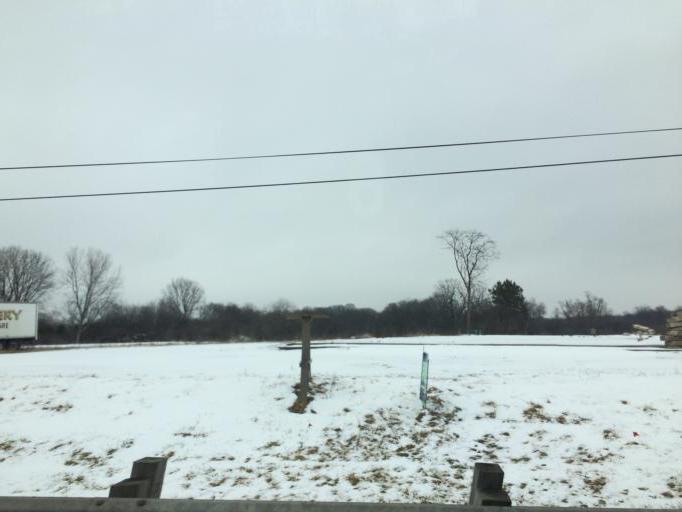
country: US
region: Illinois
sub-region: McHenry County
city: Harvard
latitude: 42.3986
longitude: -88.6128
